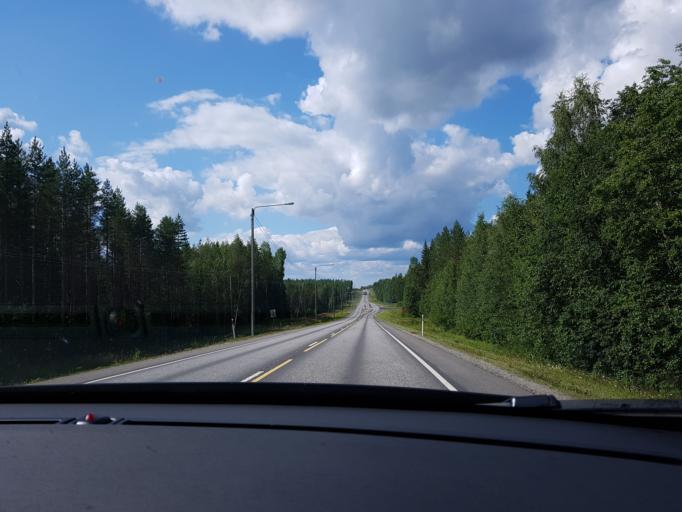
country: FI
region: Kainuu
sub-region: Kajaani
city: Ristijaervi
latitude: 64.3265
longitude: 28.0662
